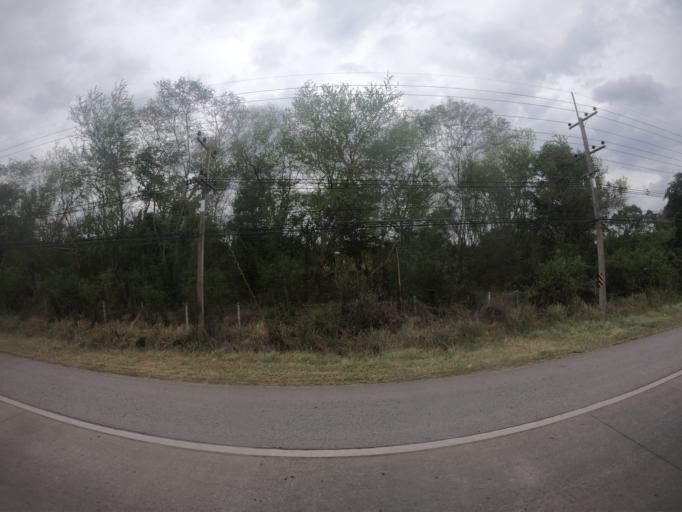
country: TH
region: Nakhon Ratchasima
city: Chok Chai
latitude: 14.7825
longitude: 102.1644
